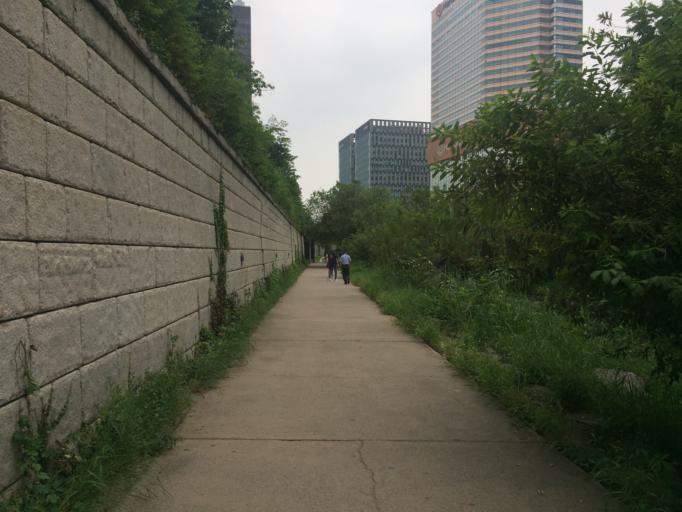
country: KR
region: Seoul
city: Seoul
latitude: 37.5685
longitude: 126.9837
